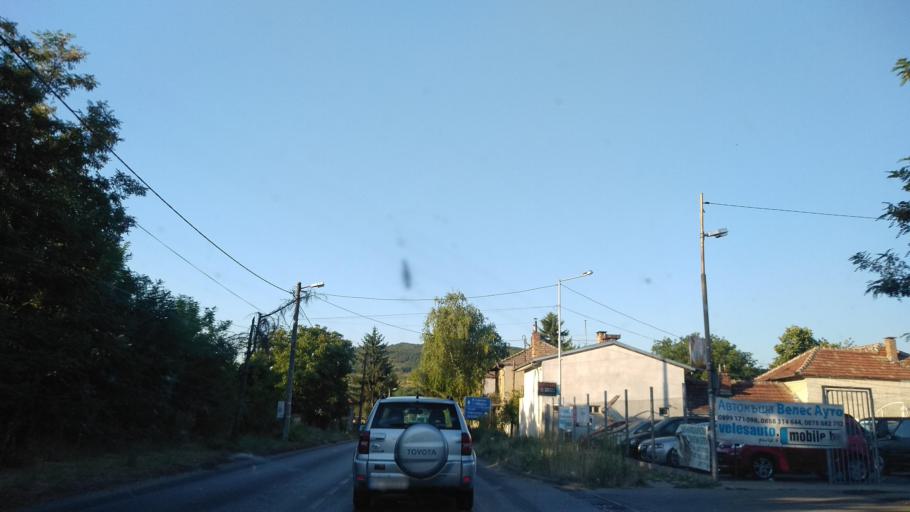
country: BG
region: Veliko Turnovo
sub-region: Obshtina Gorna Oryakhovitsa
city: Purvomaytsi
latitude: 43.1432
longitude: 25.6110
